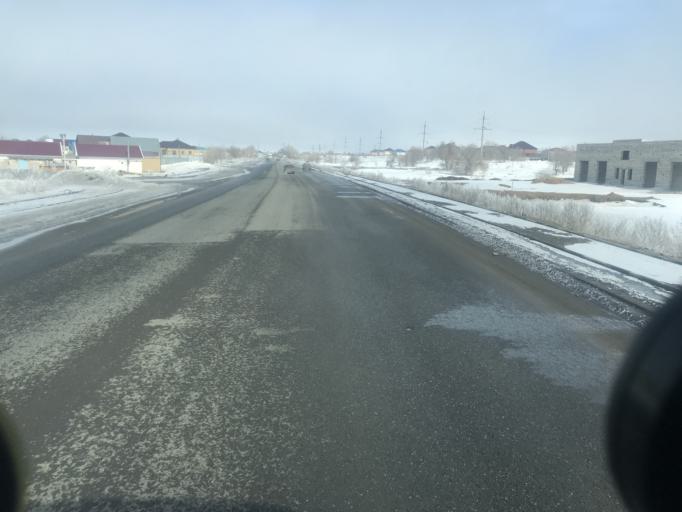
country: KZ
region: Aqtoebe
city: Aqtobe
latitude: 50.2806
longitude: 57.2816
